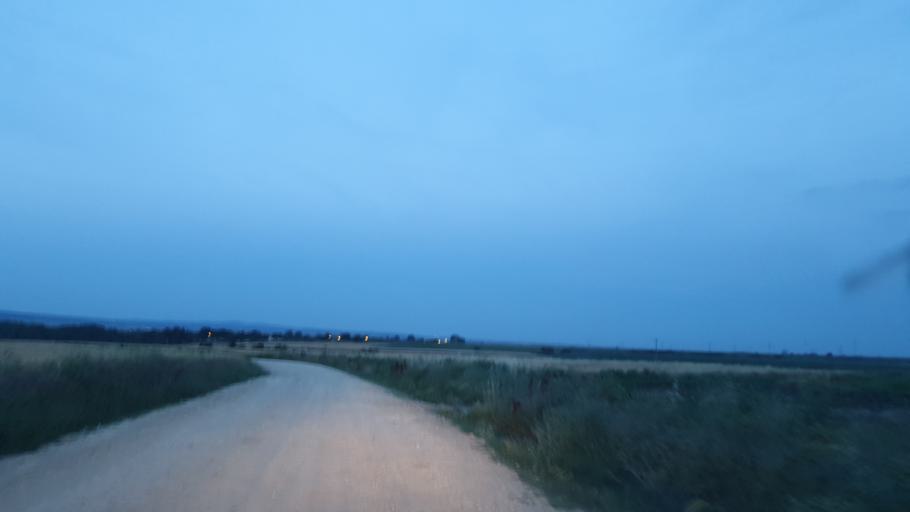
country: TR
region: Kirklareli
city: Vize
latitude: 41.5177
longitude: 27.7627
